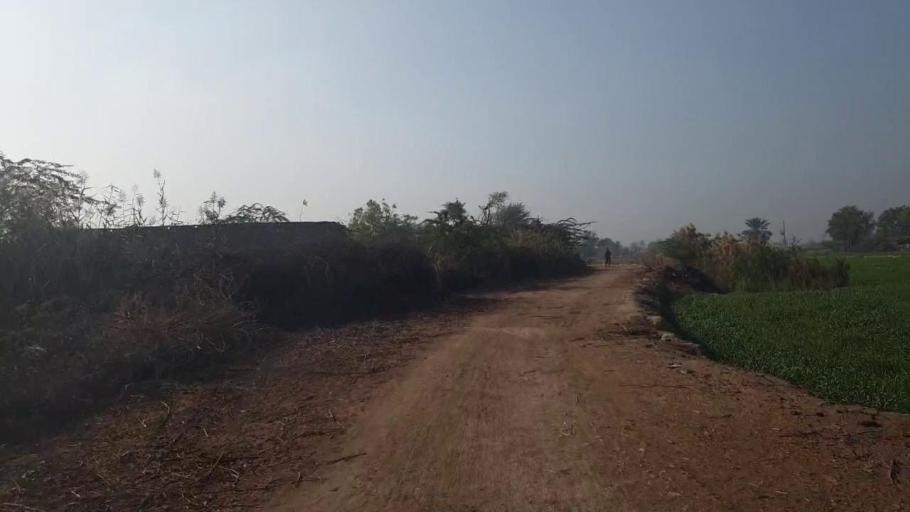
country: PK
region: Sindh
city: Shahdadpur
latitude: 25.9429
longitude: 68.5766
